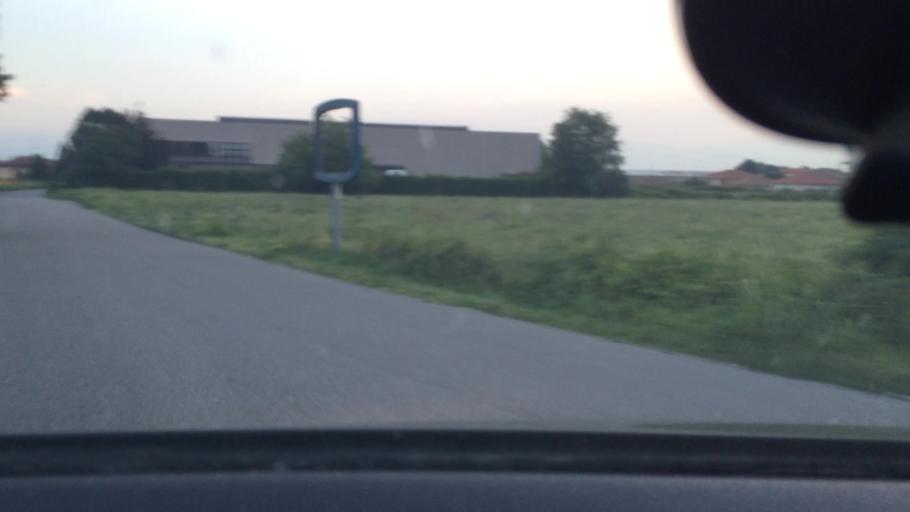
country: IT
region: Lombardy
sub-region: Provincia di Varese
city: Gerenzano
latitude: 45.6500
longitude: 8.9901
